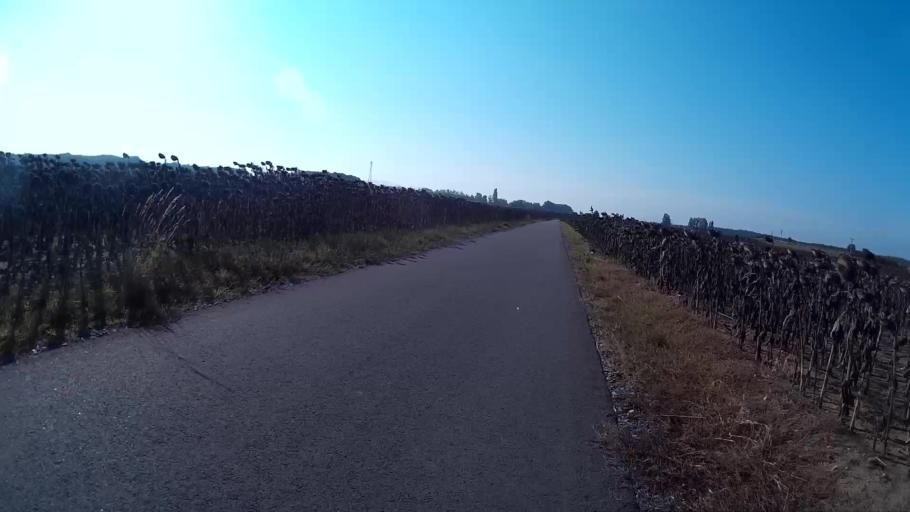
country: CZ
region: South Moravian
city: Vranovice
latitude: 48.9631
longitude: 16.5825
